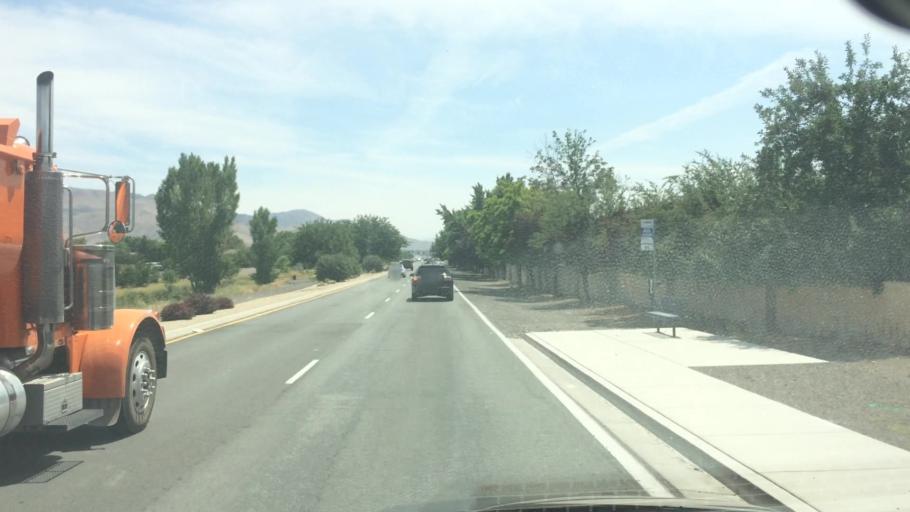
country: US
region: Nevada
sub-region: Washoe County
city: Sparks
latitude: 39.5468
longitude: -119.7155
